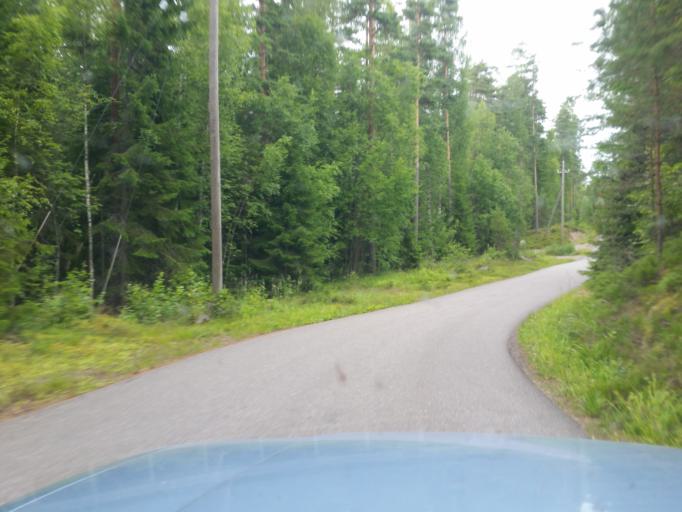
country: FI
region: Uusimaa
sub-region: Helsinki
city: Kaerkoelae
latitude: 60.5570
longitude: 24.0023
